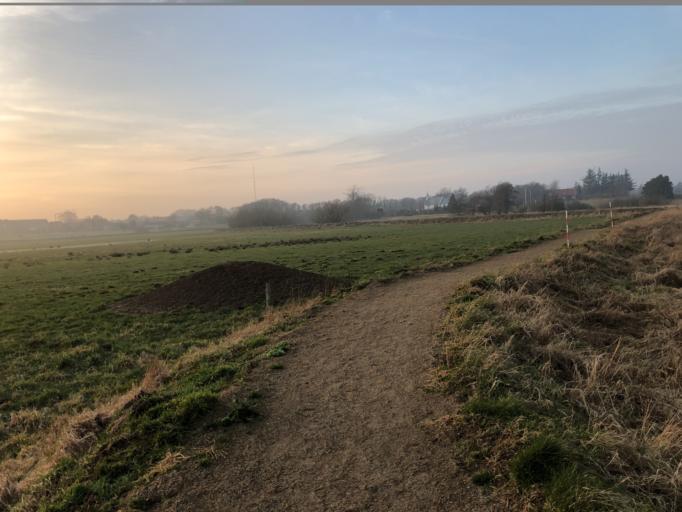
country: DK
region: Central Jutland
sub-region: Holstebro Kommune
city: Ulfborg
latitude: 56.3412
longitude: 8.3569
